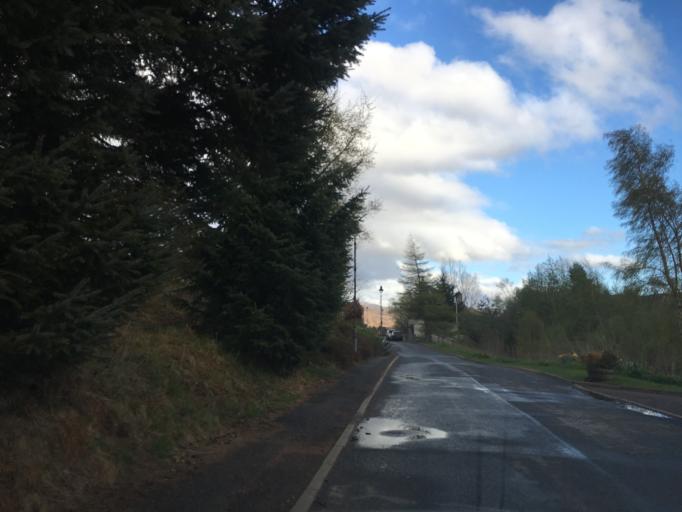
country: GB
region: Scotland
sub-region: Highland
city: Kingussie
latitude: 57.0201
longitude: -4.2851
